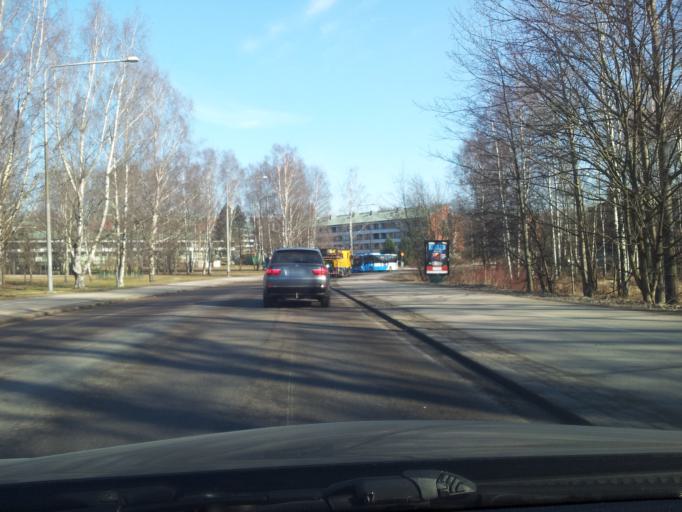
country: FI
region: Uusimaa
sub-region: Helsinki
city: Teekkarikylae
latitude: 60.2075
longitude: 24.8841
